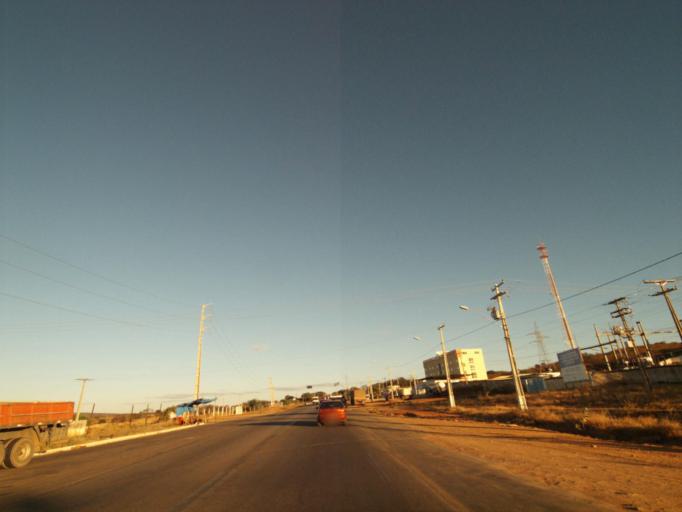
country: BR
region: Bahia
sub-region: Brumado
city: Brumado
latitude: -14.2052
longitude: -41.6542
